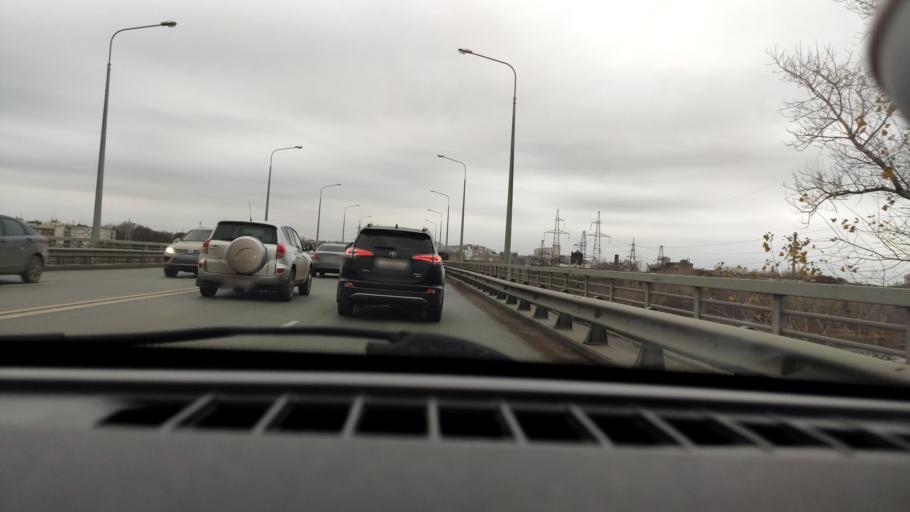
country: RU
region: Samara
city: Samara
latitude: 53.1676
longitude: 50.1983
